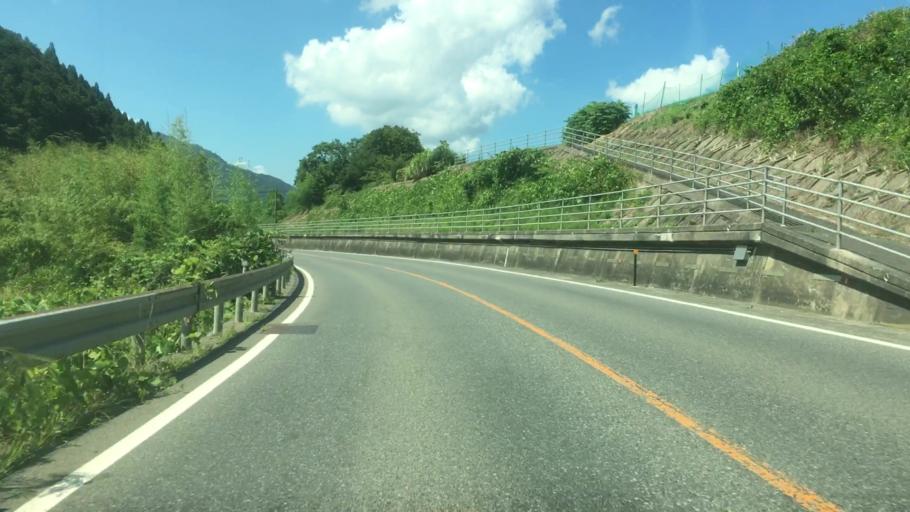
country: JP
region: Tottori
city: Tottori
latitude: 35.2438
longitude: 134.2295
